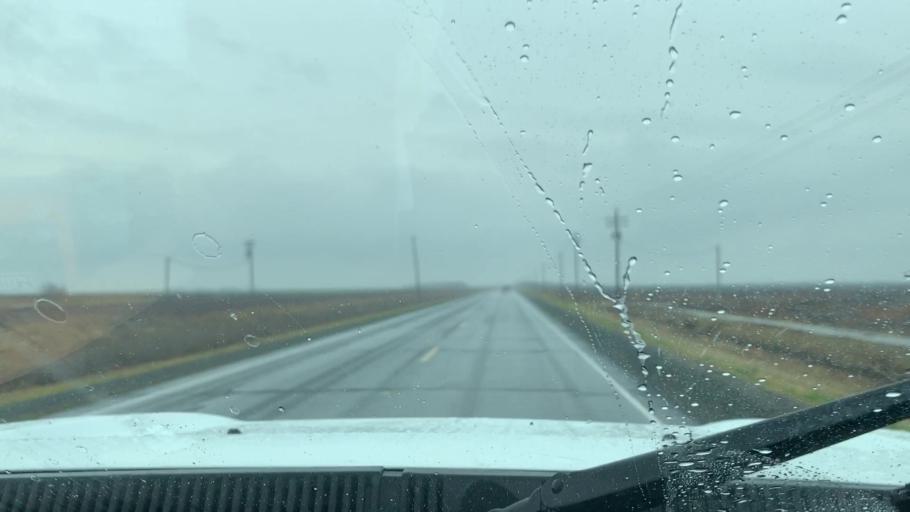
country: US
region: California
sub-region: Tulare County
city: Alpaugh
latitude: 35.9338
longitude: -119.4362
